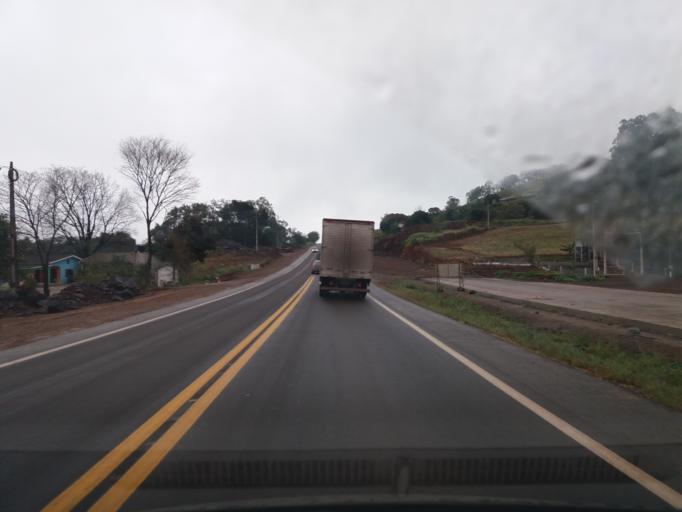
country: BR
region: Parana
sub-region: Realeza
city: Realeza
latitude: -25.4265
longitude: -53.5762
